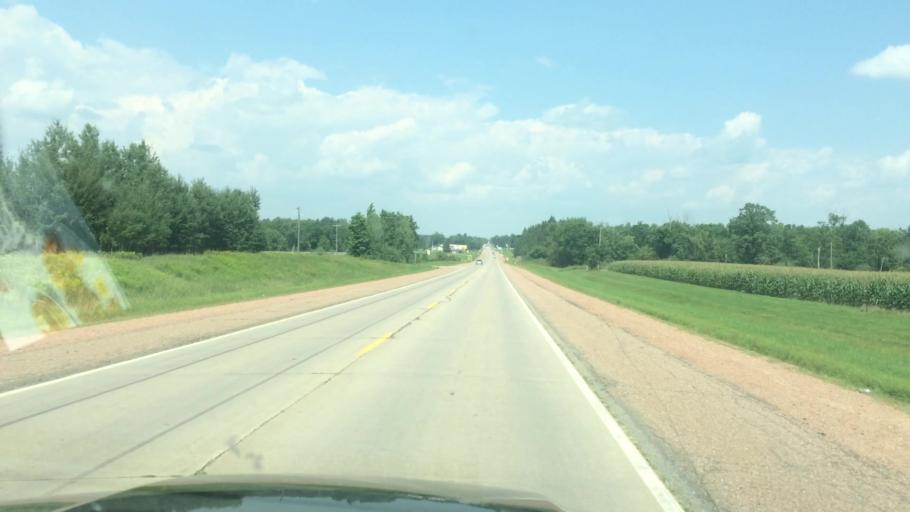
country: US
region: Wisconsin
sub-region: Clark County
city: Colby
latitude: 44.8860
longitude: -90.3154
